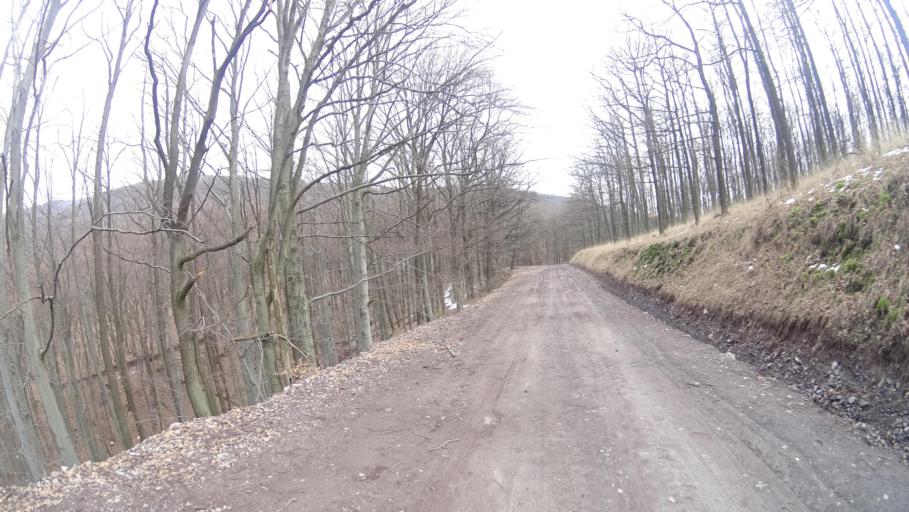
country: HU
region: Pest
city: Szob
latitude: 47.9079
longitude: 18.8996
